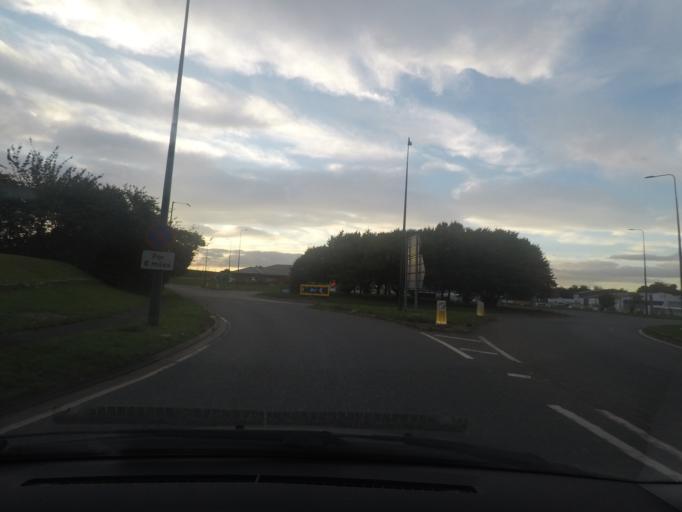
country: GB
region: England
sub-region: North East Lincolnshire
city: Laceby
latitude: 53.5352
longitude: -0.1797
